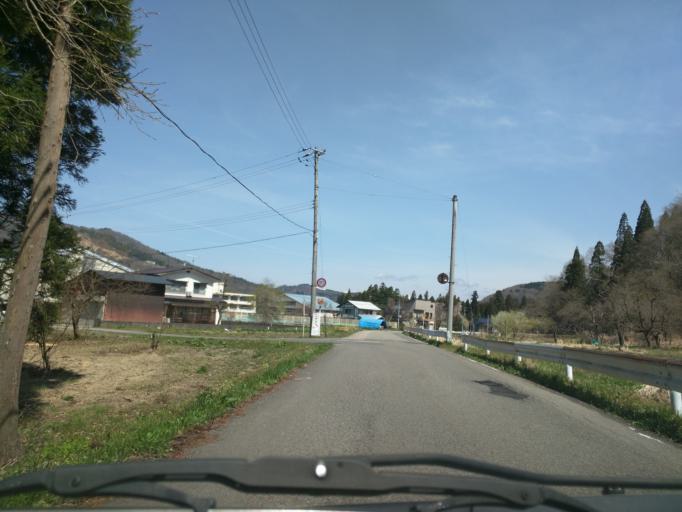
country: JP
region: Fukushima
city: Kitakata
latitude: 37.5229
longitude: 139.7225
